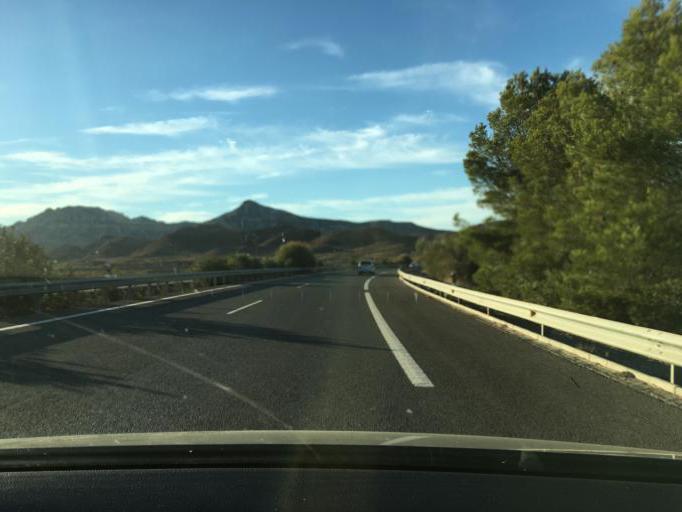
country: ES
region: Andalusia
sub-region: Provincia de Almeria
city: Sorbas
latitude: 37.0496
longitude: -2.0484
